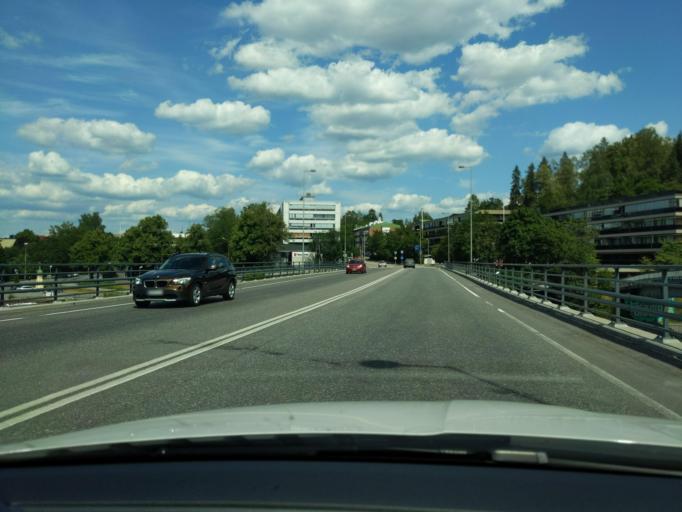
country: FI
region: Paijanne Tavastia
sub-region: Lahti
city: Heinola
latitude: 61.1988
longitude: 26.0328
